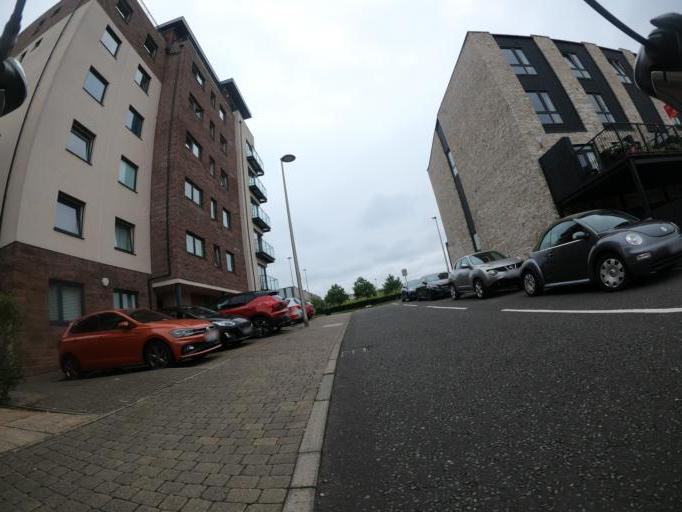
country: GB
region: Scotland
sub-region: Edinburgh
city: Edinburgh
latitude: 55.9816
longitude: -3.2345
